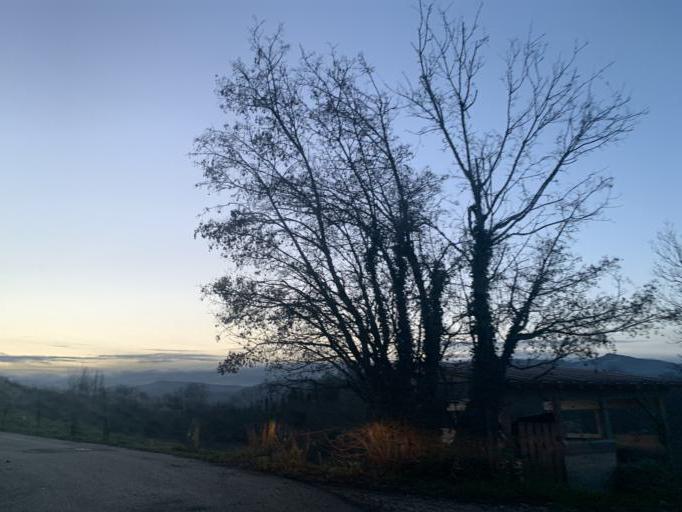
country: FR
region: Rhone-Alpes
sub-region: Departement de l'Ain
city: Belley
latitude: 45.7740
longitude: 5.7036
